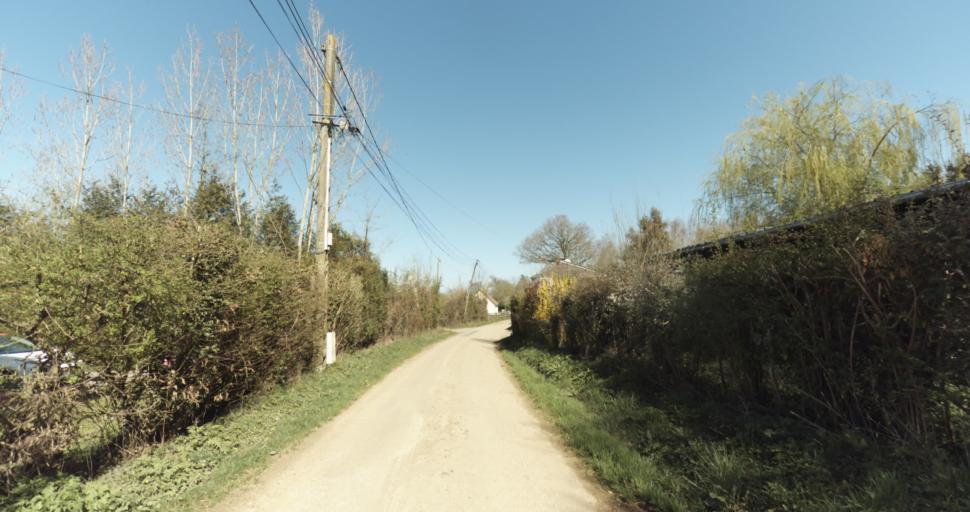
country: FR
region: Lower Normandy
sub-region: Departement du Calvados
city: Livarot
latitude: 49.0178
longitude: 0.1042
